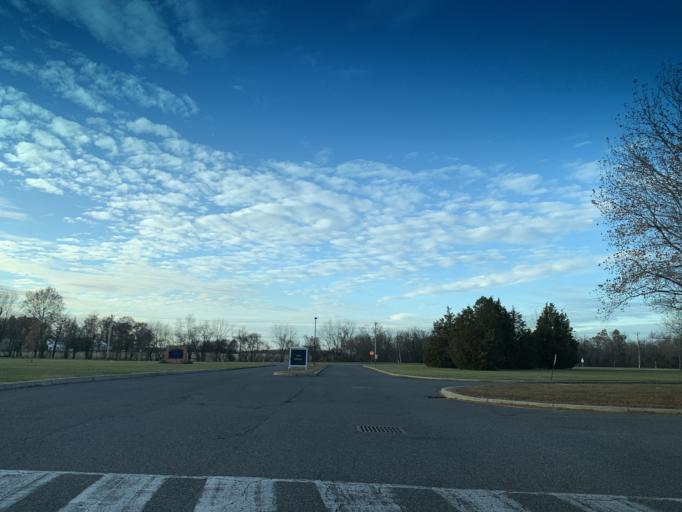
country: US
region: Maryland
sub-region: Kent County
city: Chestertown
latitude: 39.2852
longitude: -76.0934
